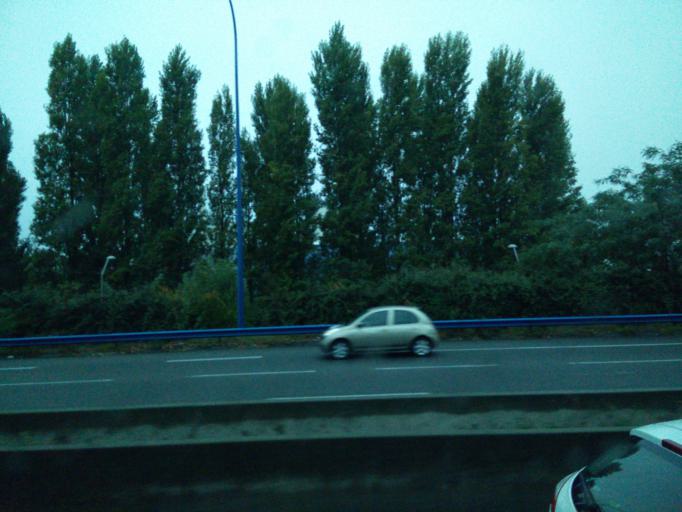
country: FR
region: Midi-Pyrenees
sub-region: Departement de la Haute-Garonne
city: Blagnac
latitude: 43.6281
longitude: 1.4201
